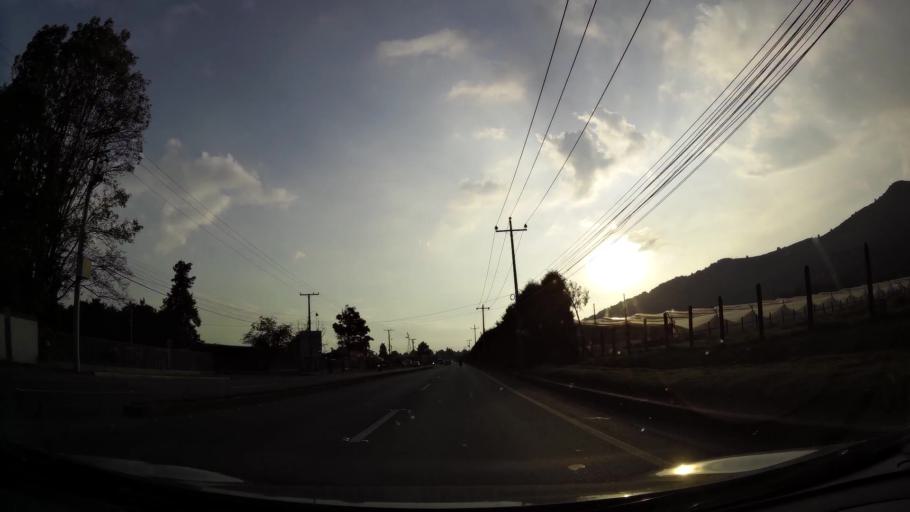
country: CO
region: Cundinamarca
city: Cota
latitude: 4.7817
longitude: -74.1336
